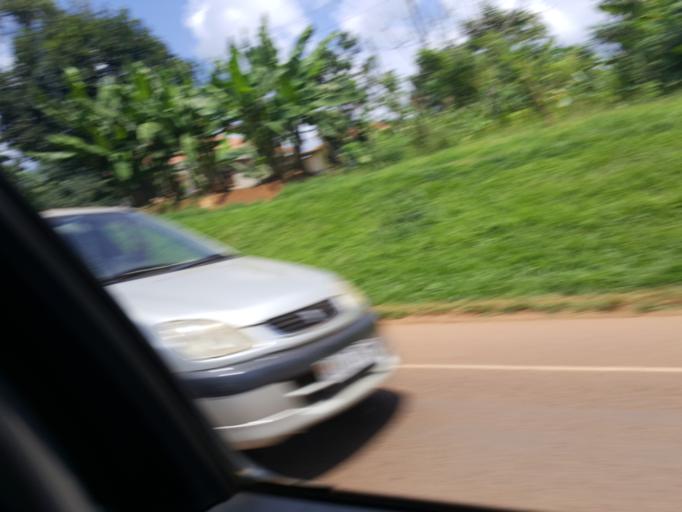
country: UG
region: Central Region
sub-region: Wakiso District
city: Kajansi
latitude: 0.1518
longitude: 32.5458
